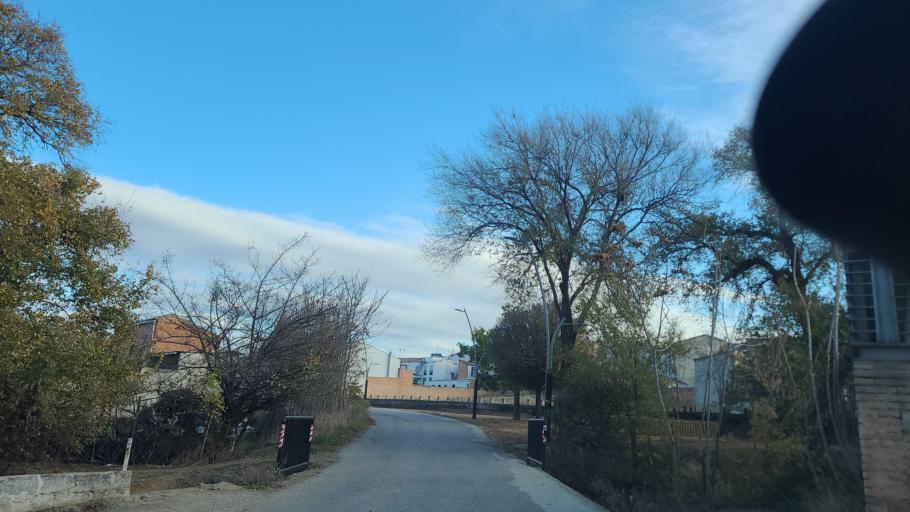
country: ES
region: Andalusia
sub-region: Provincia de Jaen
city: Mengibar
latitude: 37.9737
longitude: -3.8098
